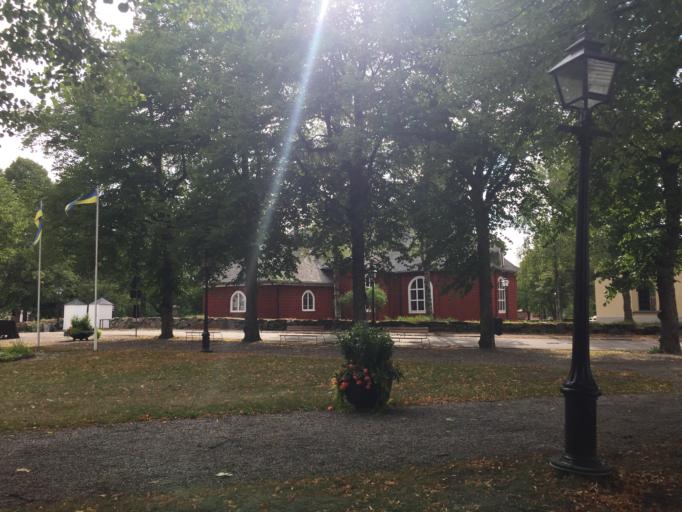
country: SE
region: OErebro
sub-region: Hallefors Kommun
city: Haellefors
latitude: 59.7059
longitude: 14.5373
